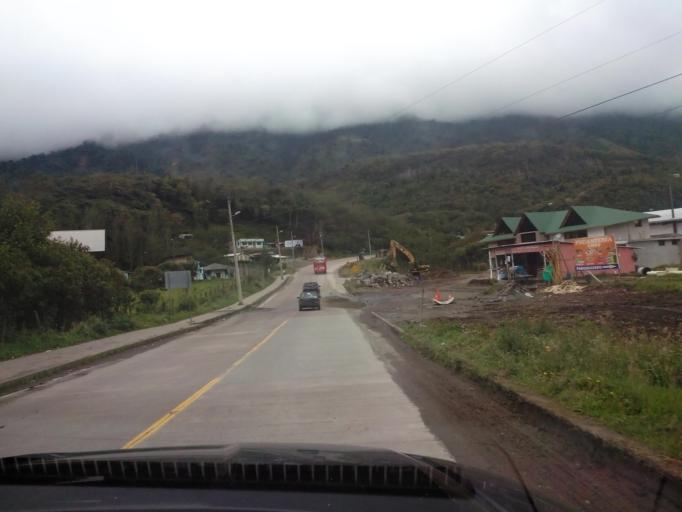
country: EC
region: Pichincha
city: Sangolqui
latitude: -0.3793
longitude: -78.1390
